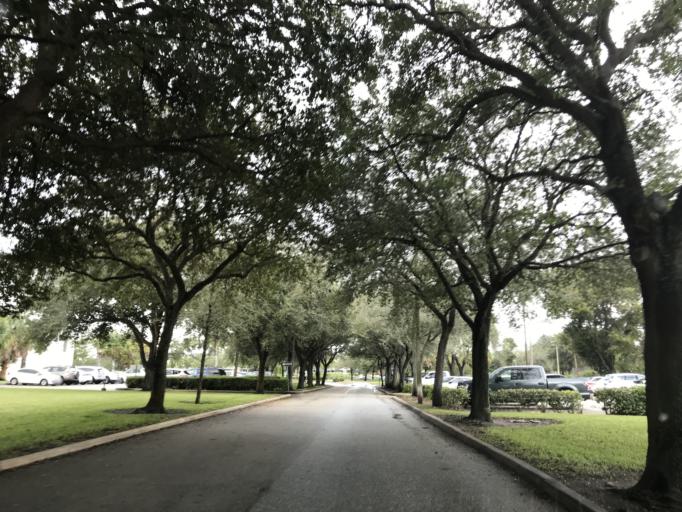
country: US
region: Florida
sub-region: Palm Beach County
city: Delray Beach
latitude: 26.4556
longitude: -80.0920
